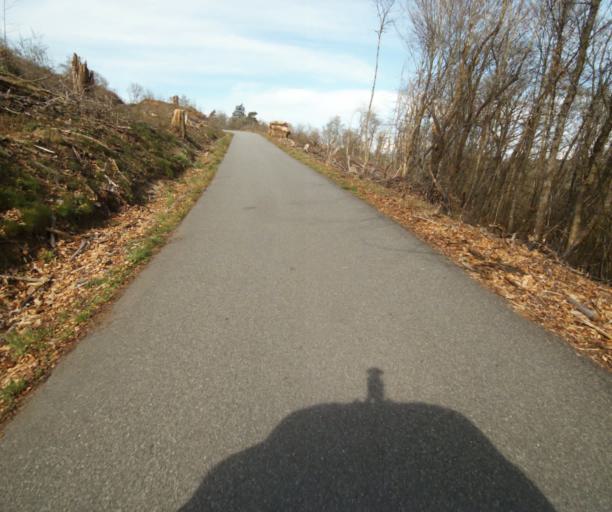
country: FR
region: Limousin
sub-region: Departement de la Correze
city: Correze
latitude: 45.3438
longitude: 1.8476
